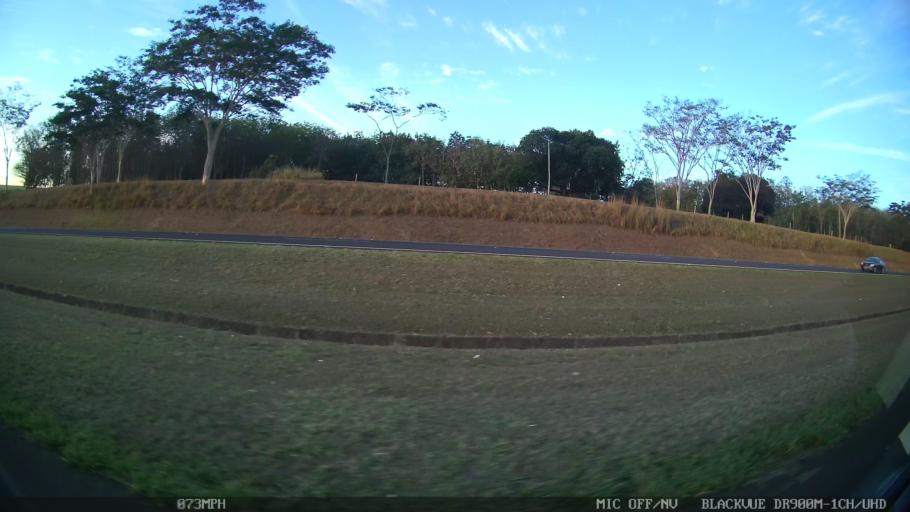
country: BR
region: Sao Paulo
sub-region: Pindorama
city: Pindorama
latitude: -21.2244
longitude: -48.9155
